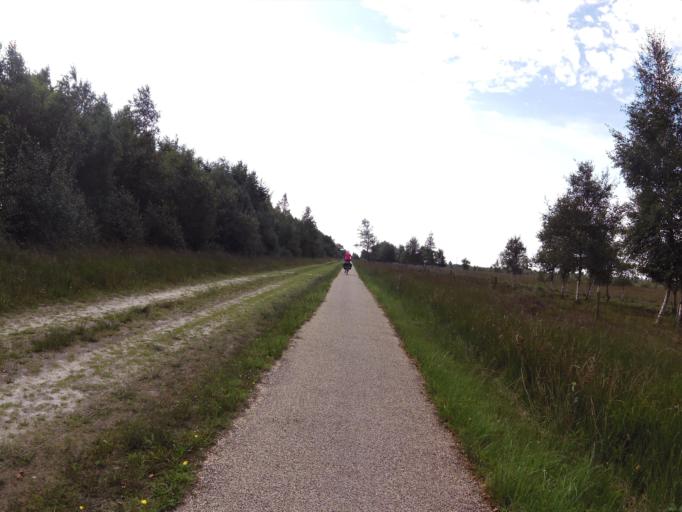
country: DE
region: Lower Saxony
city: Twist
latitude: 52.6811
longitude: 7.0590
